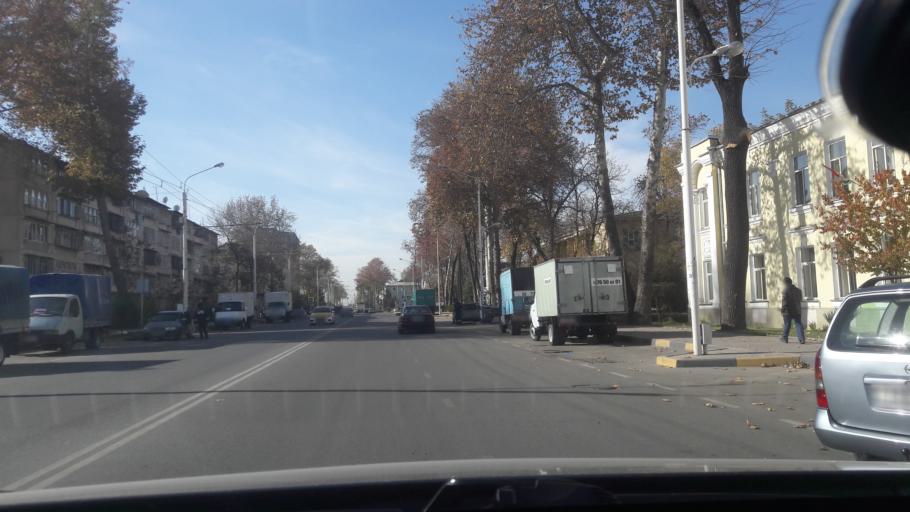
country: TJ
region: Dushanbe
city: Dushanbe
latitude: 38.5581
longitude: 68.7977
